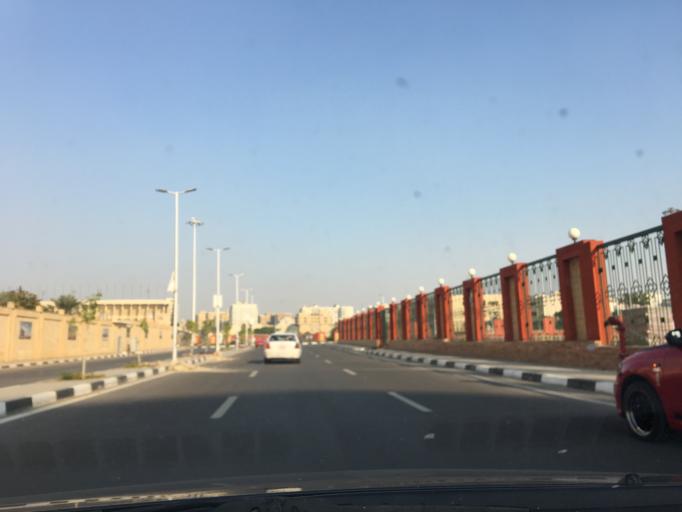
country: EG
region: Muhafazat al Qahirah
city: Cairo
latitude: 30.0731
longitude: 31.3092
